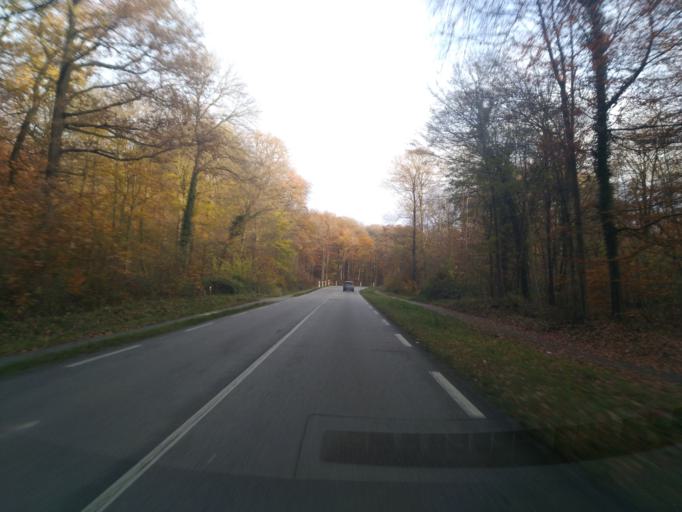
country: FR
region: Ile-de-France
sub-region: Departement des Yvelines
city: Saint-Nom-la-Breteche
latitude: 48.8701
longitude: 2.0391
